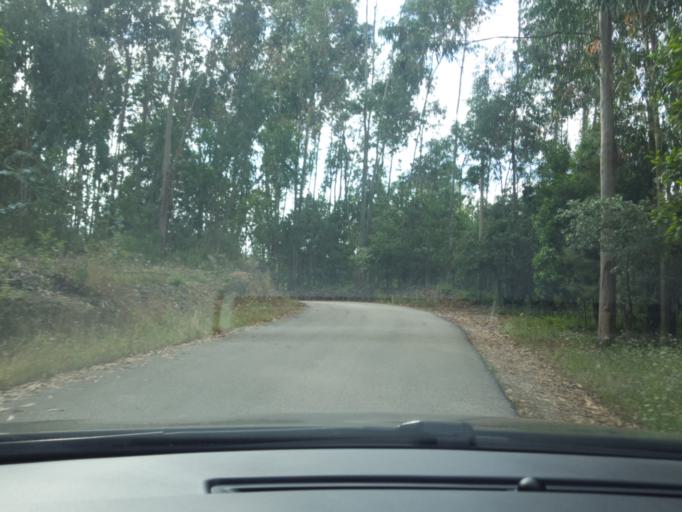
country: PT
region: Leiria
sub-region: Leiria
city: Caranguejeira
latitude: 39.7939
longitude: -8.7495
